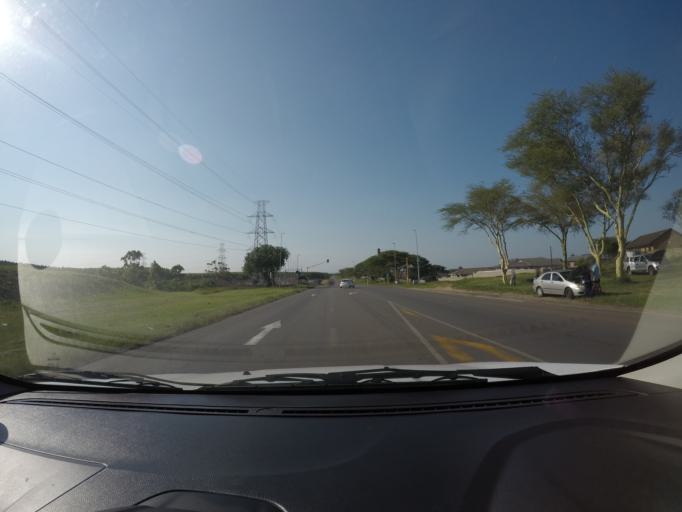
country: ZA
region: KwaZulu-Natal
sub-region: uThungulu District Municipality
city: Richards Bay
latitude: -28.7261
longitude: 32.0357
